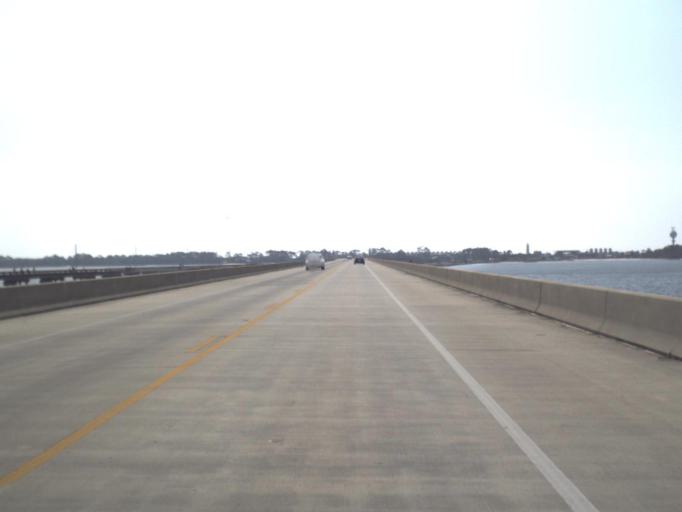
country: US
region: Florida
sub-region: Franklin County
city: Eastpoint
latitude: 29.6755
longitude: -84.8718
